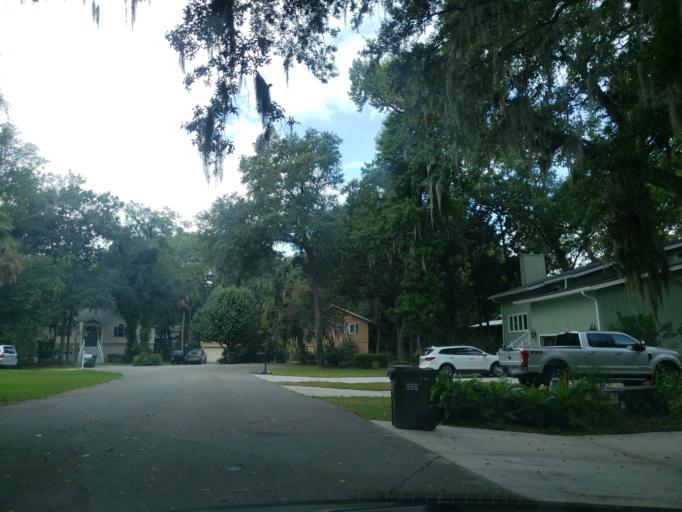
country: US
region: Georgia
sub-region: Chatham County
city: Wilmington Island
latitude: 32.0076
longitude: -80.9598
